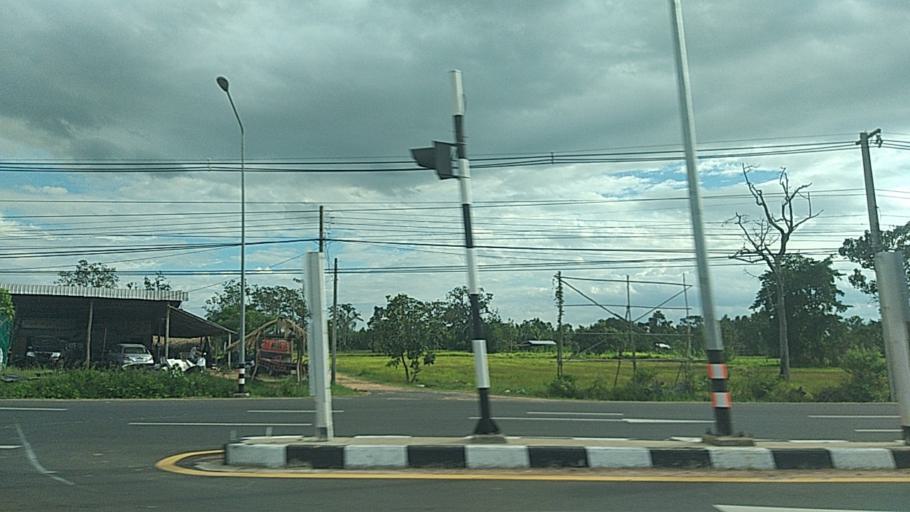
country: TH
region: Surin
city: Prasat
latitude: 14.6069
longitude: 103.4236
